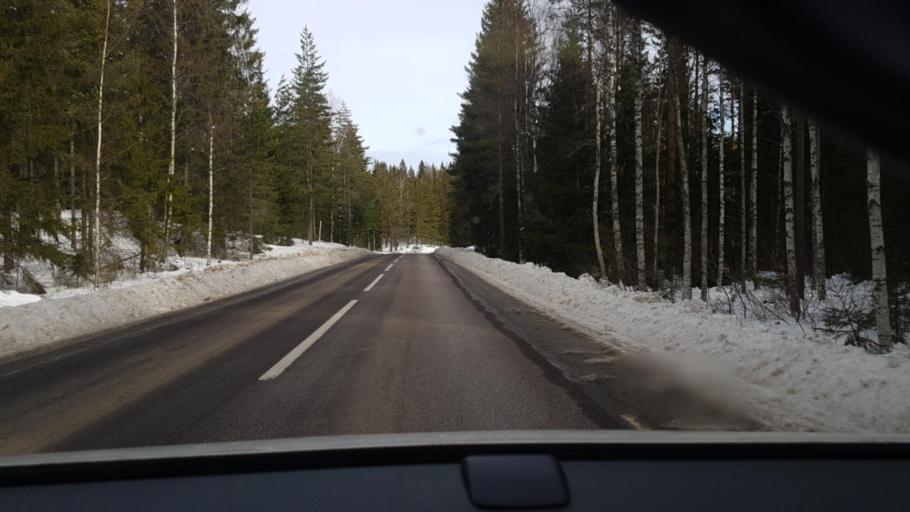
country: SE
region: Vaermland
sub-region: Eda Kommun
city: Amotfors
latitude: 59.6516
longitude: 12.3680
